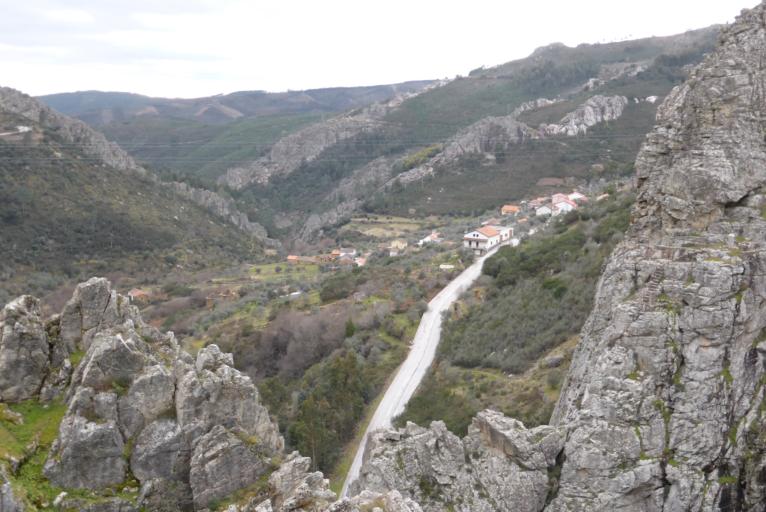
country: PT
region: Coimbra
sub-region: Pampilhosa da Serra
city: Pampilhosa da Serra
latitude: 40.0900
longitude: -7.8577
